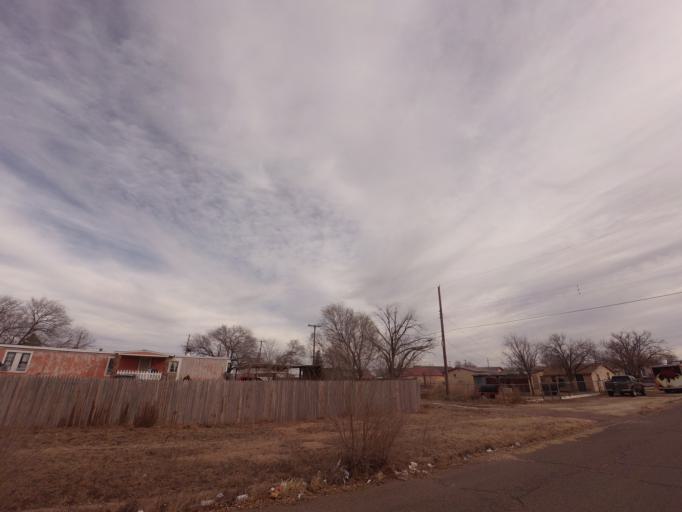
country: US
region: New Mexico
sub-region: Curry County
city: Clovis
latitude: 34.3996
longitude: -103.2288
